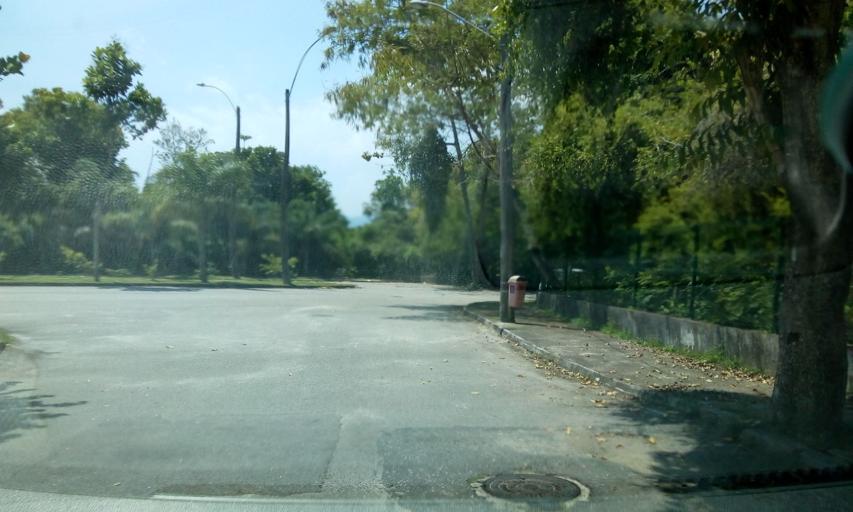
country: BR
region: Rio de Janeiro
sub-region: Nilopolis
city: Nilopolis
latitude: -23.0252
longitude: -43.4665
